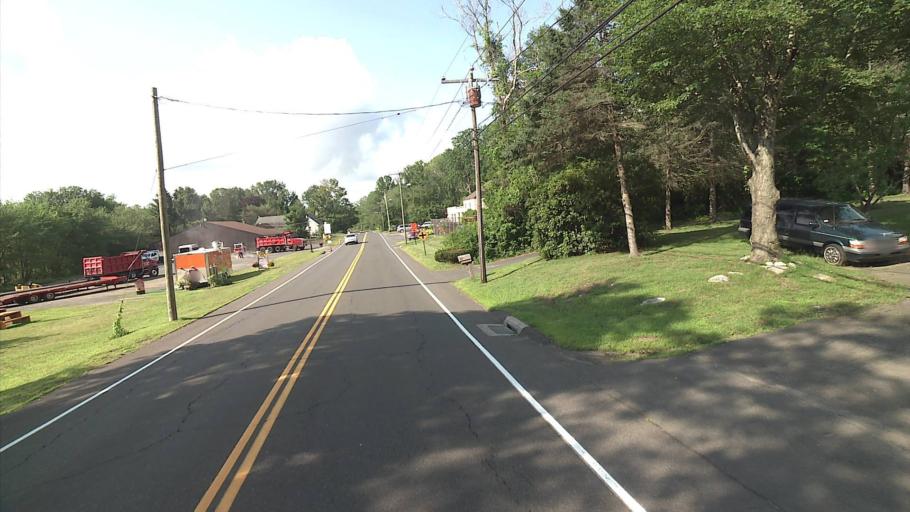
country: US
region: Connecticut
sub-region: Middlesex County
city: Higganum
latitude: 41.4330
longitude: -72.5588
